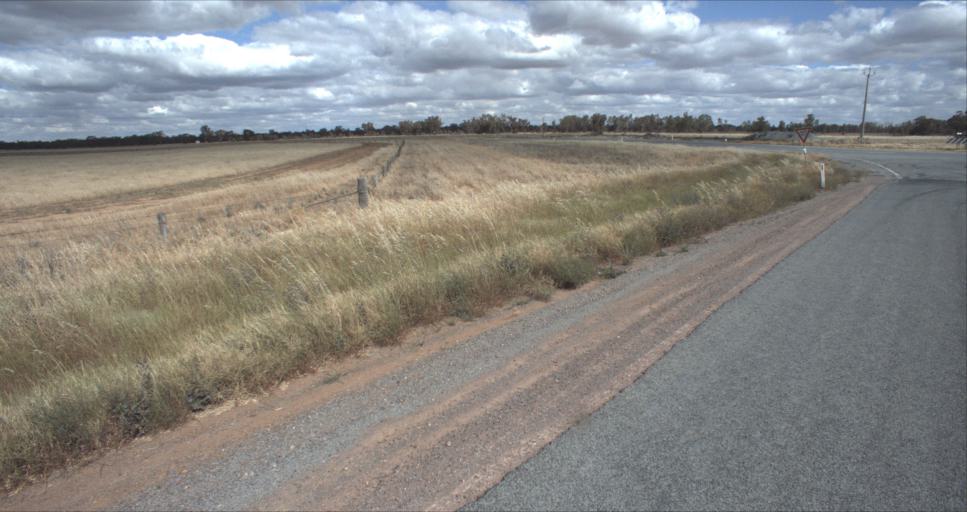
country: AU
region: New South Wales
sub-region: Leeton
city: Leeton
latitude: -34.6970
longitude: 146.3426
